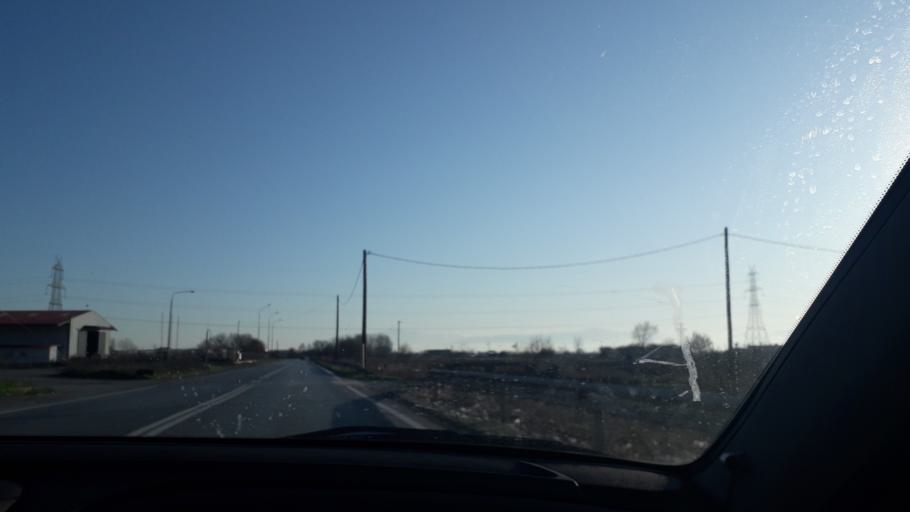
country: GR
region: Central Macedonia
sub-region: Nomos Pellis
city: Giannitsa
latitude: 40.7649
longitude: 22.4059
